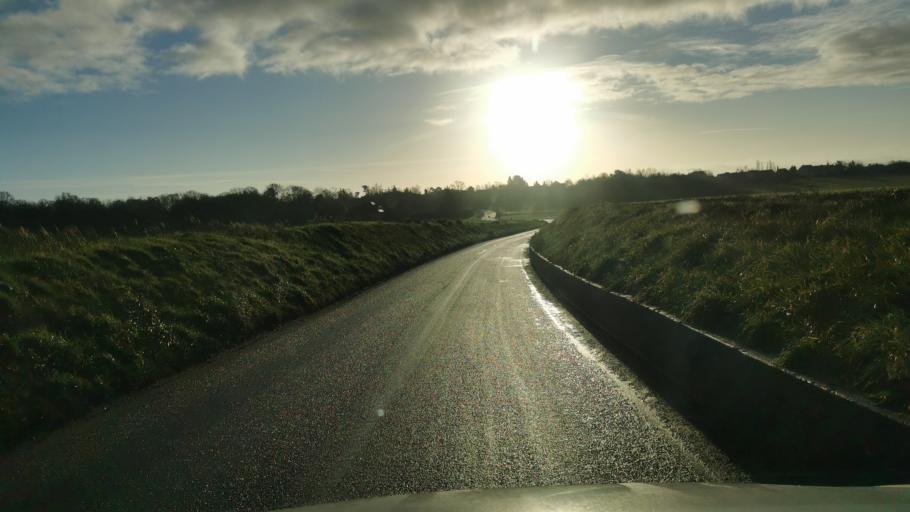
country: FR
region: Ile-de-France
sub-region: Departement des Yvelines
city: Bazainville
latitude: 48.8294
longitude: 1.6277
